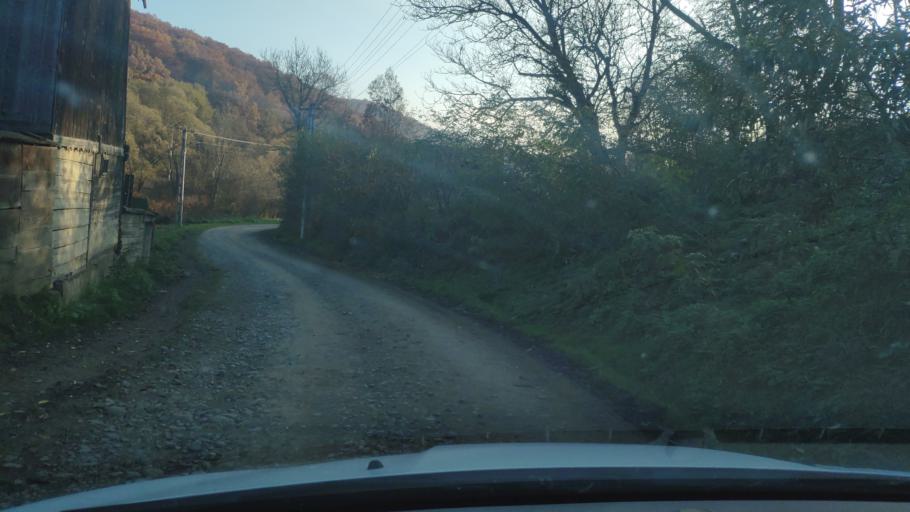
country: RO
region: Mures
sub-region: Comuna Ghindari
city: Ghindari
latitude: 46.5227
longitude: 24.9153
